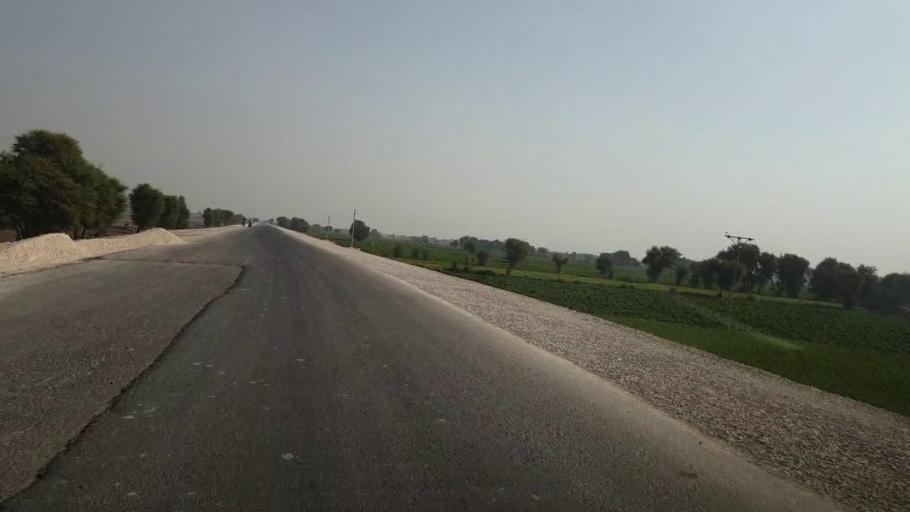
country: PK
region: Sindh
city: Bhan
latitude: 26.5609
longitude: 67.7742
